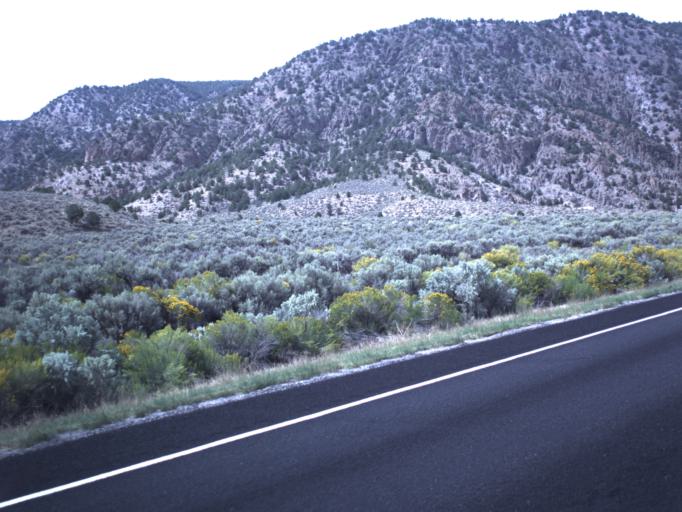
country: US
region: Utah
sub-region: Piute County
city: Junction
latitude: 38.0600
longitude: -112.3486
